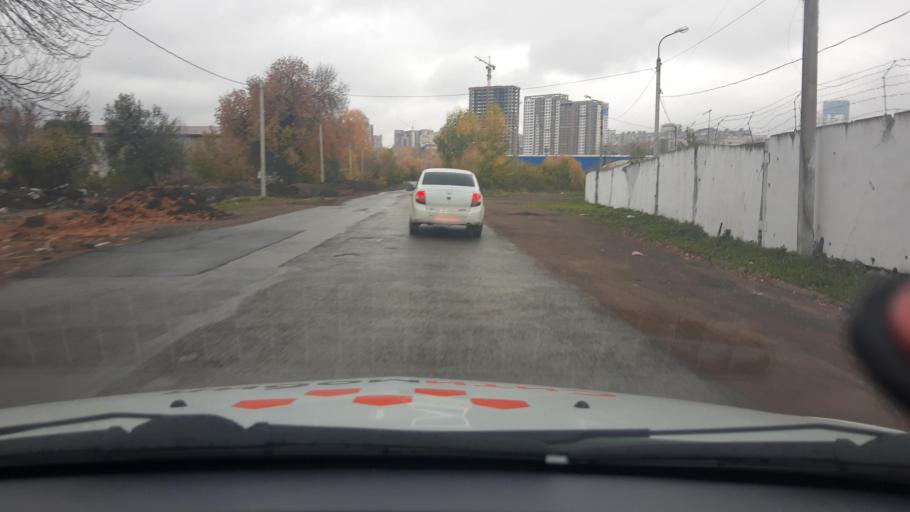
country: RU
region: Bashkortostan
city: Ufa
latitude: 54.7831
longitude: 56.0592
